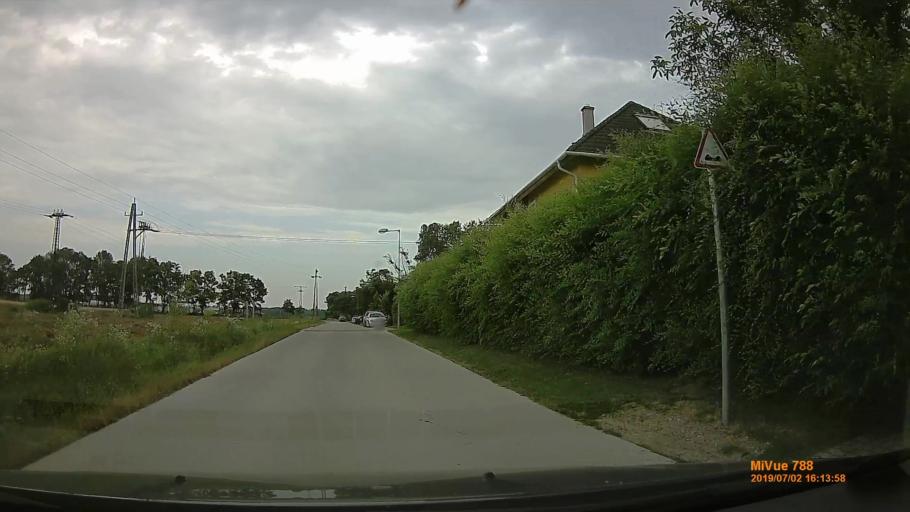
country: HU
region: Gyor-Moson-Sopron
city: Mosonmagyarovar
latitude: 47.8841
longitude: 17.2878
